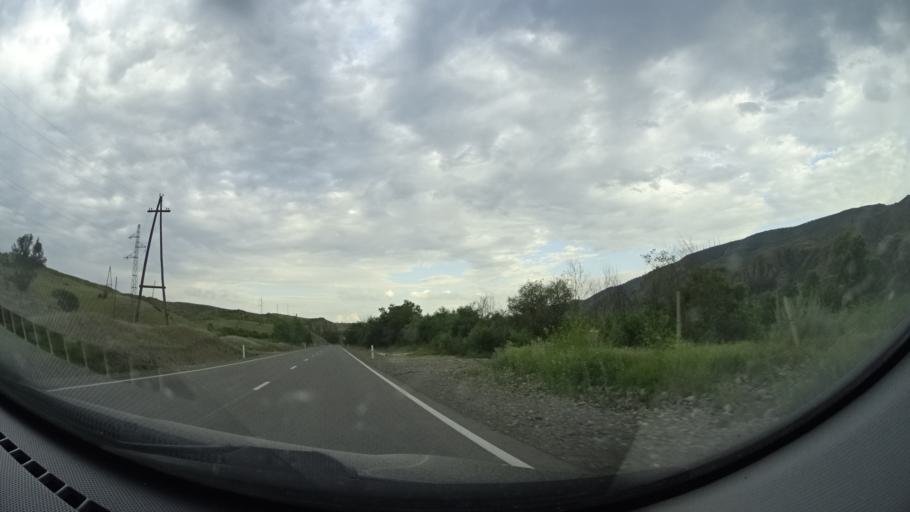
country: GE
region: Samtskhe-Javakheti
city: Akhaltsikhe
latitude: 41.6480
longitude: 42.9389
